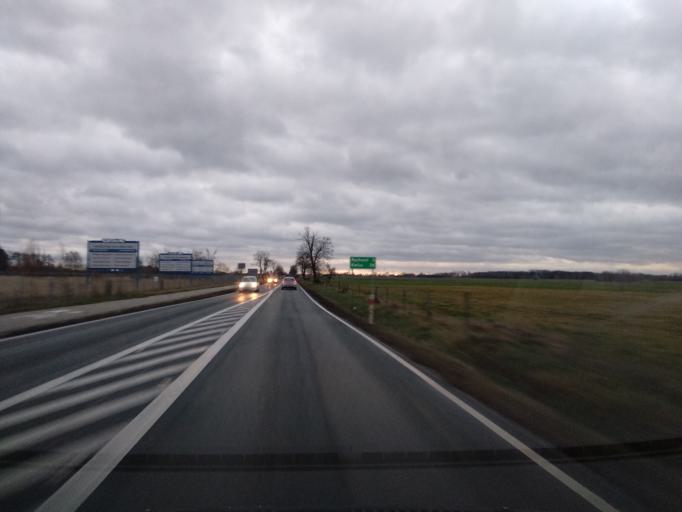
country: PL
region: Greater Poland Voivodeship
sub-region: Powiat koninski
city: Rychwal
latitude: 52.0943
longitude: 18.1661
